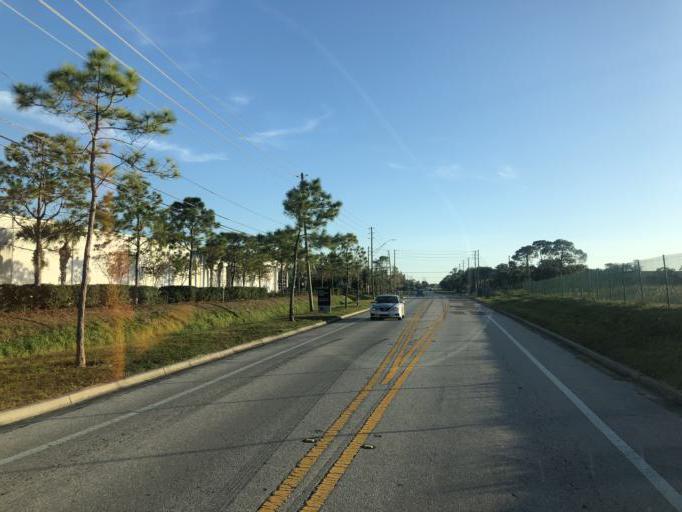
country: US
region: Florida
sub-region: Pinellas County
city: Gandy
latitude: 27.8662
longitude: -82.6553
